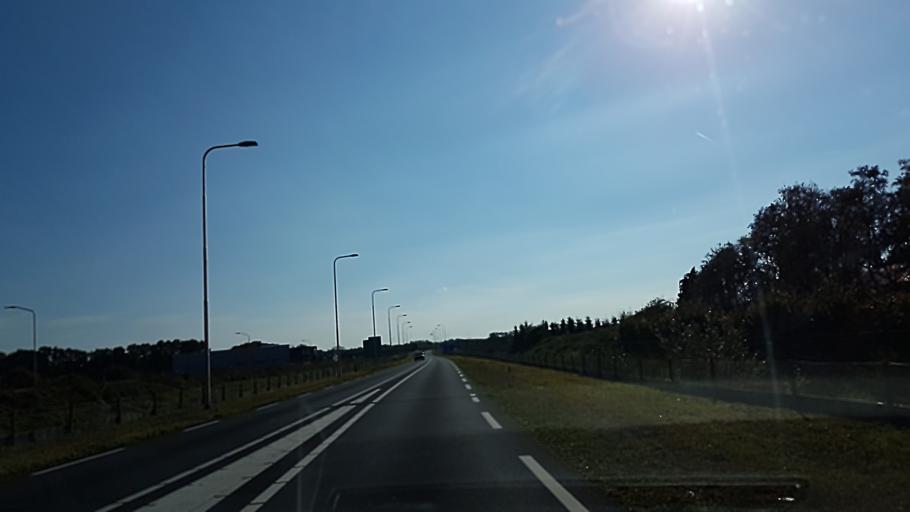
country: NL
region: North Brabant
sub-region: Gemeente Woensdrecht
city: Woensdrecht
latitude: 51.4281
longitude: 4.3409
